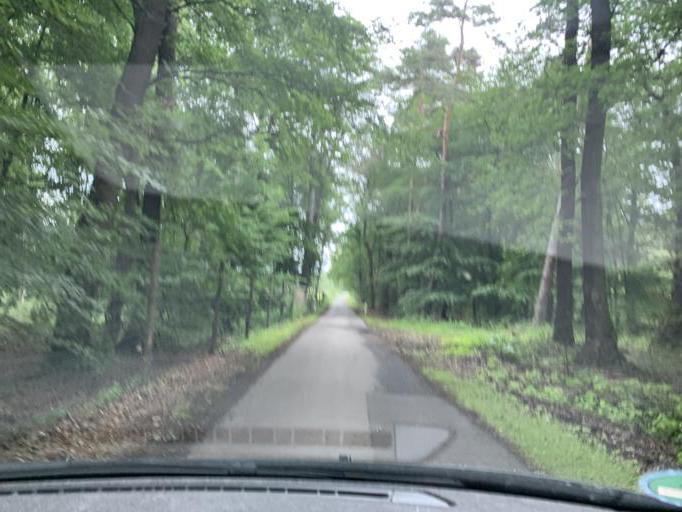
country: DE
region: North Rhine-Westphalia
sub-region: Regierungsbezirk Koln
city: Merzenich
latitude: 50.8722
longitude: 6.5147
